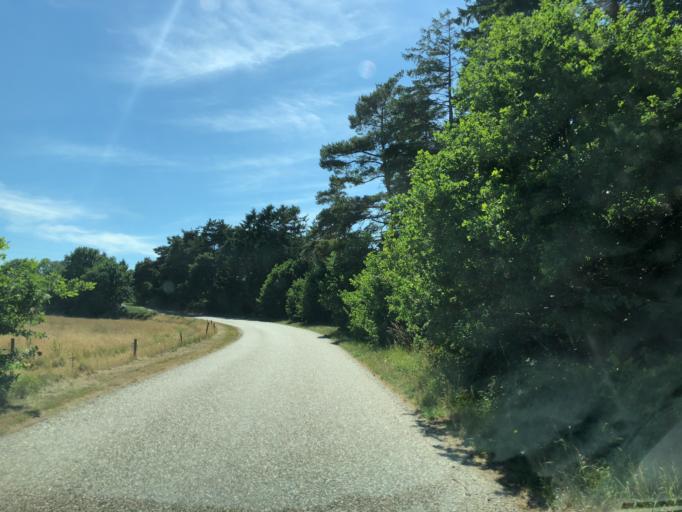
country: DK
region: Central Jutland
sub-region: Holstebro Kommune
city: Vinderup
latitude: 56.4128
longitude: 8.9269
